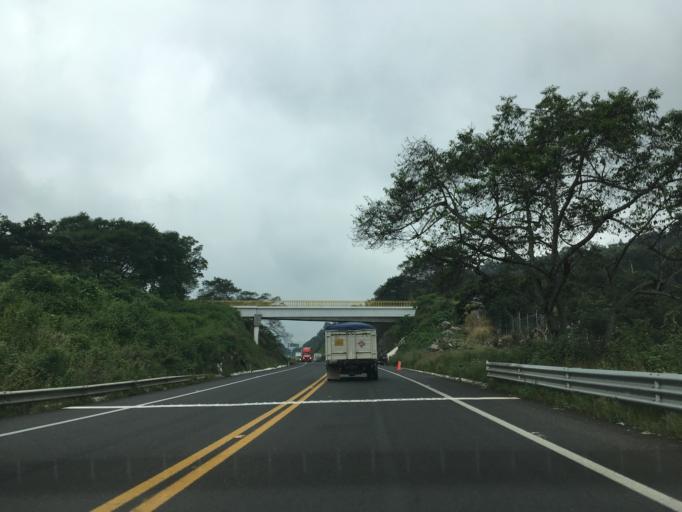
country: MX
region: Michoacan
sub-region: Ziracuaretiro
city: Patuan
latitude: 19.4170
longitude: -101.9443
